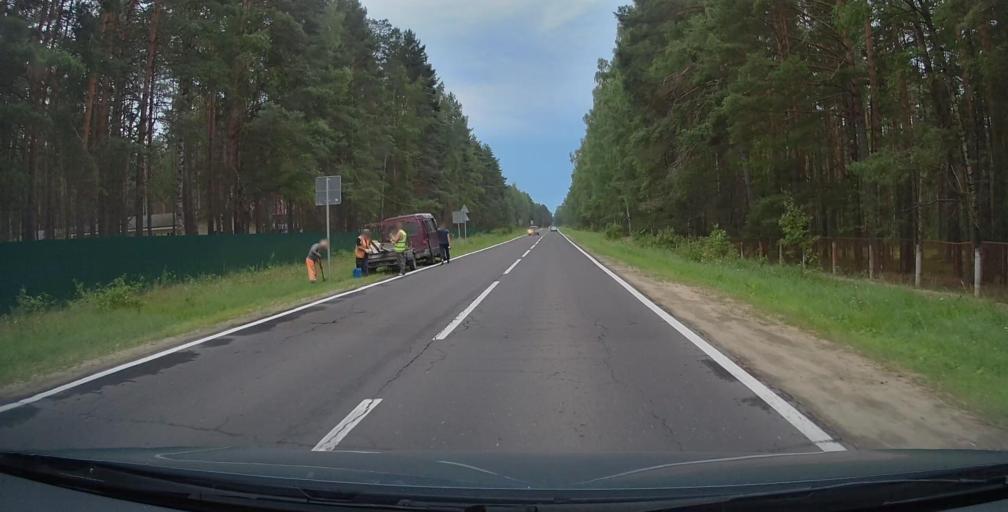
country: RU
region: Jaroslavl
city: Myshkin
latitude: 57.7879
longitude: 38.4935
